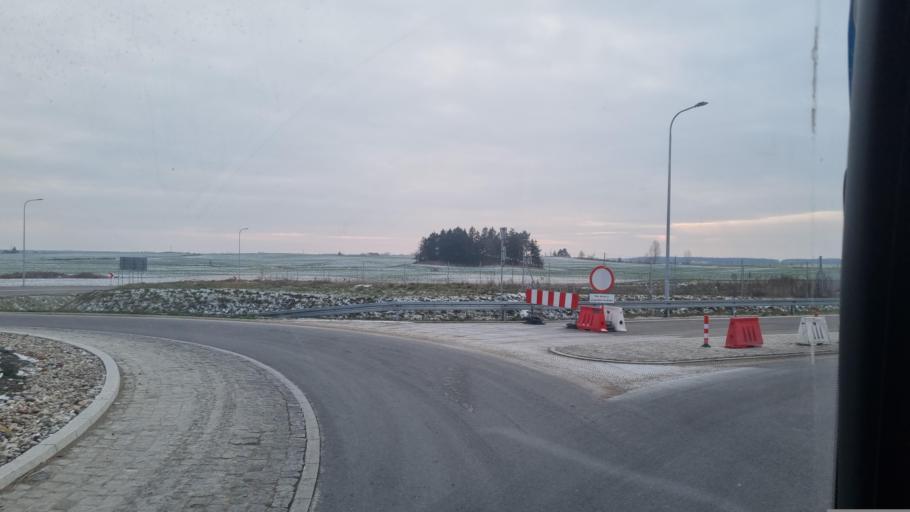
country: PL
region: Podlasie
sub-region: Powiat grajewski
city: Rajgrod
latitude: 53.8549
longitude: 22.5855
